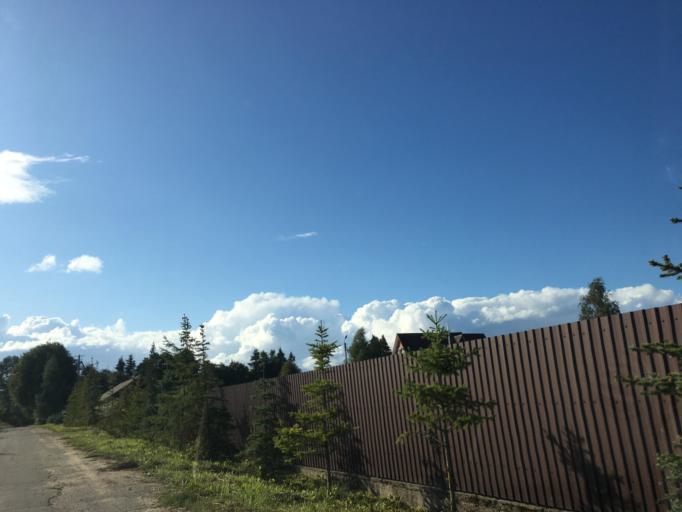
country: RU
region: Pskov
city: Izborsk
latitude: 57.7701
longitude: 27.9812
